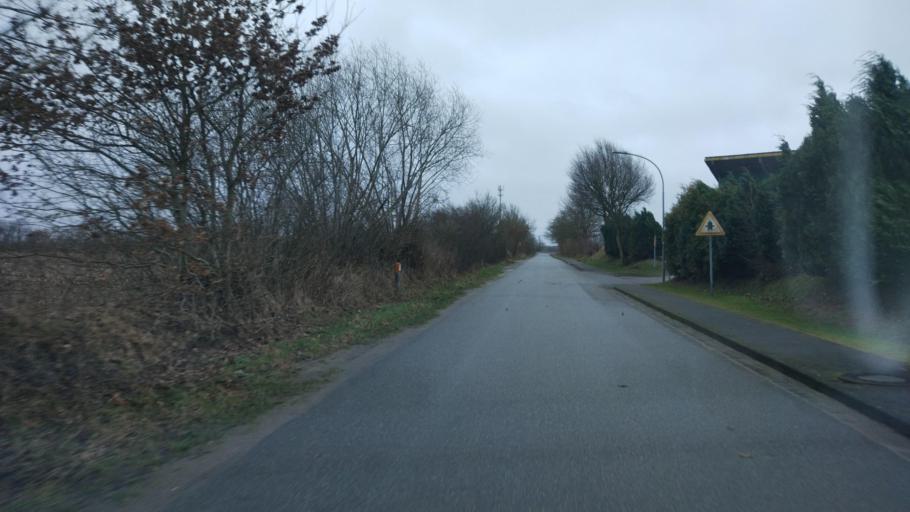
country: DE
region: Schleswig-Holstein
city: Ellingstedt
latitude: 54.4726
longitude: 9.4158
